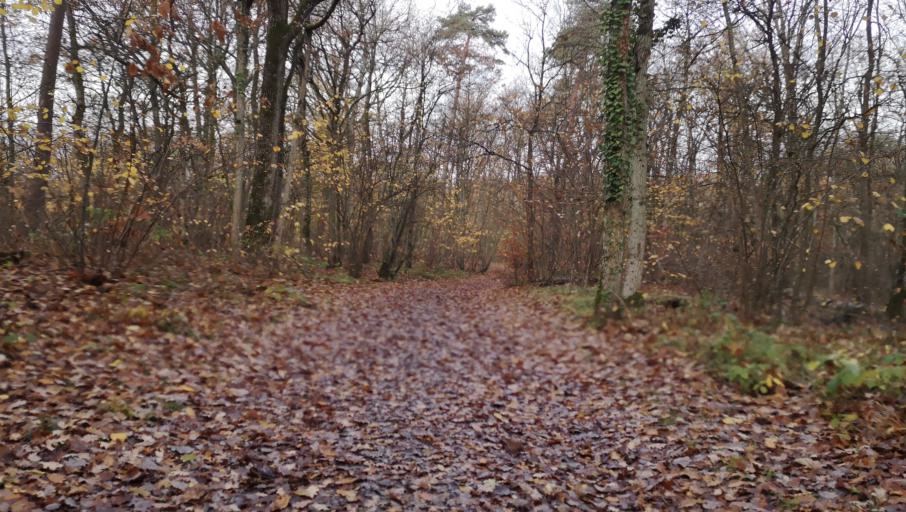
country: FR
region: Centre
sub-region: Departement du Loiret
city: Semoy
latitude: 47.9421
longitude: 1.9658
